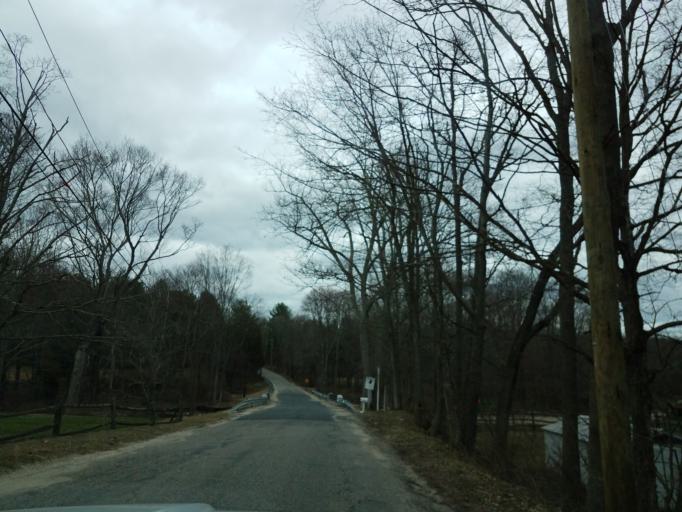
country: US
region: Connecticut
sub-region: Tolland County
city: Coventry Lake
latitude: 41.7605
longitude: -72.3985
